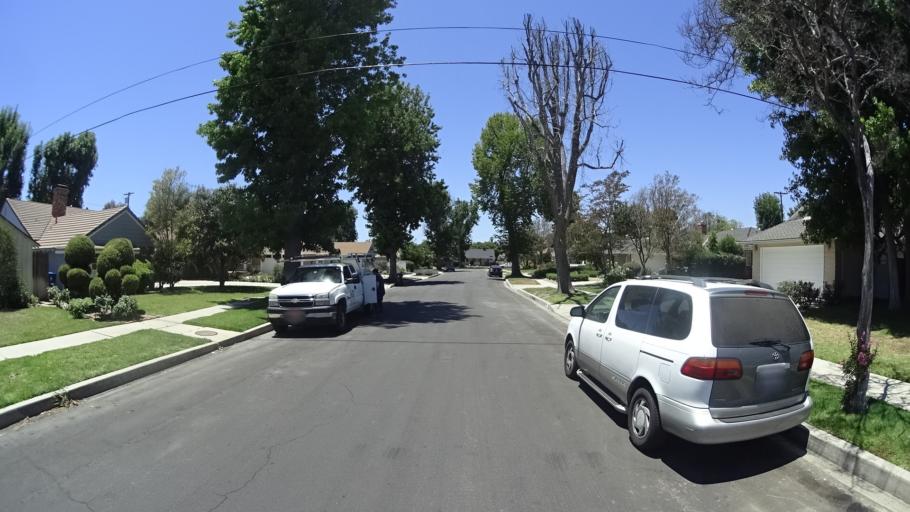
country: US
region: California
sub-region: Los Angeles County
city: Northridge
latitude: 34.1988
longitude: -118.5073
